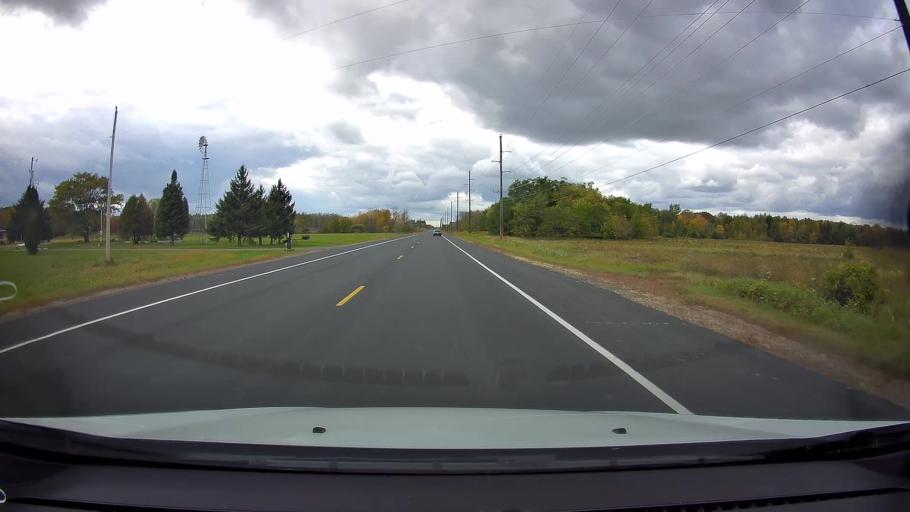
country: US
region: Minnesota
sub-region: Chisago County
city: Shafer
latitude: 45.3973
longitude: -92.7544
